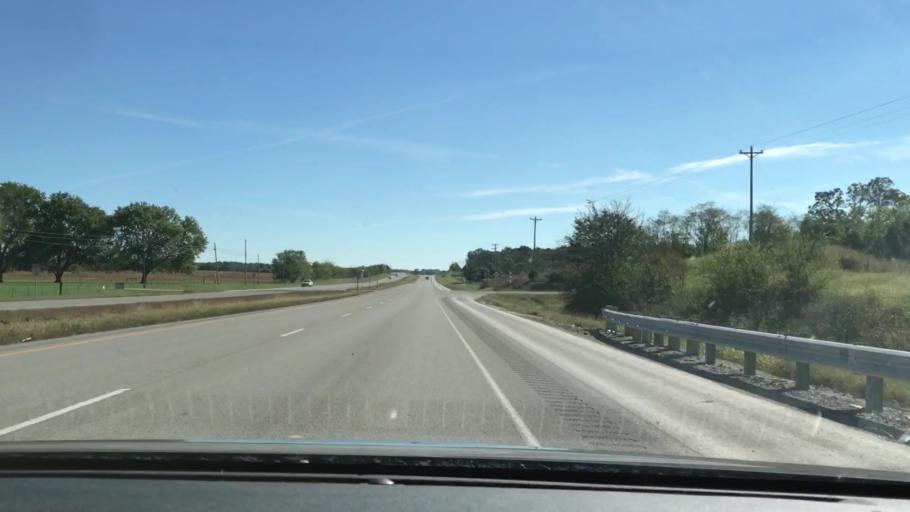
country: US
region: Kentucky
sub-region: Christian County
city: Hopkinsville
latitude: 36.8497
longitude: -87.3509
